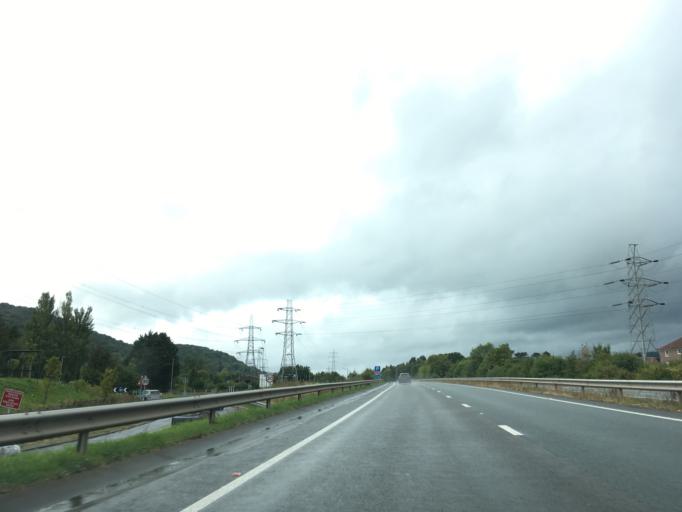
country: GB
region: Wales
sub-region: Monmouthshire
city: Abergavenny
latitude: 51.8144
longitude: -3.0242
